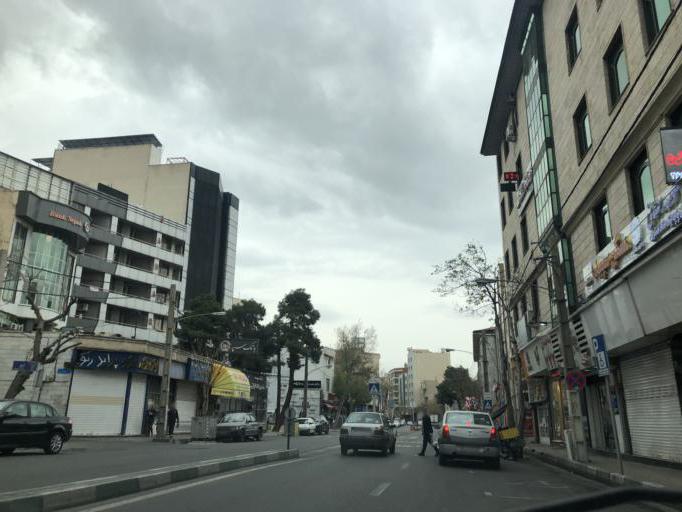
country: IR
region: Tehran
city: Tajrish
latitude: 35.7803
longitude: 51.4541
